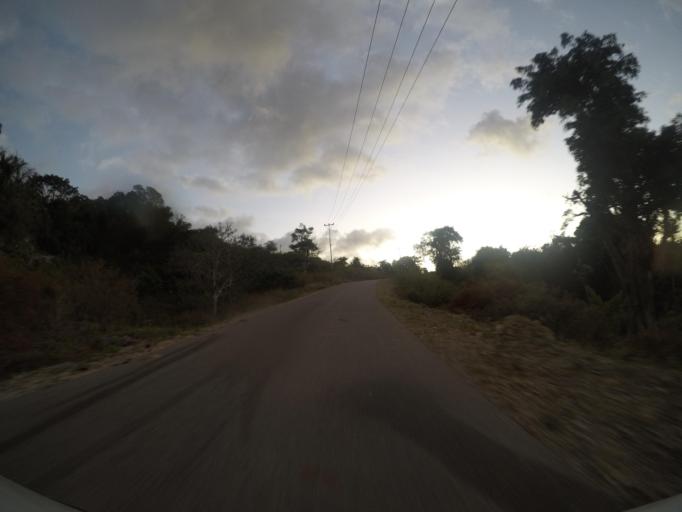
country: TL
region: Lautem
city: Lospalos
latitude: -8.3646
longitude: 127.0475
